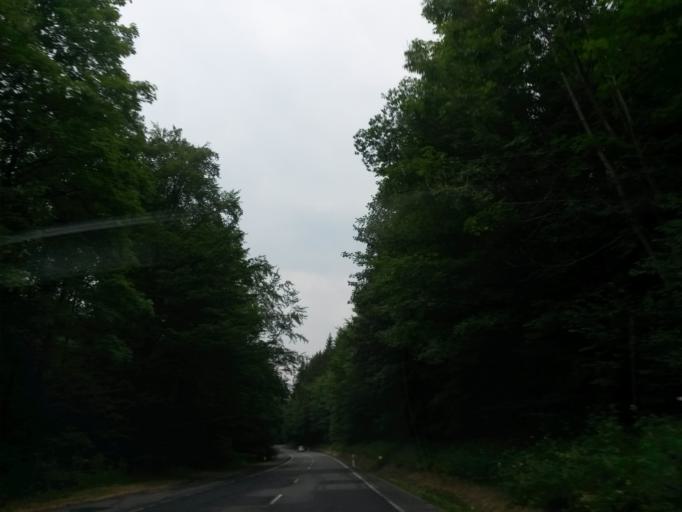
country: DE
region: North Rhine-Westphalia
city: Meinerzhagen
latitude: 51.0849
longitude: 7.6484
